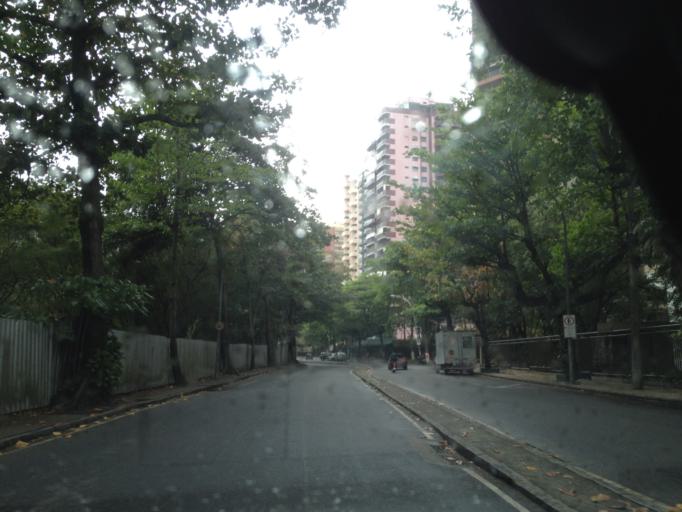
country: BR
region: Rio de Janeiro
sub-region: Rio De Janeiro
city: Rio de Janeiro
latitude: -23.0060
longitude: -43.3282
